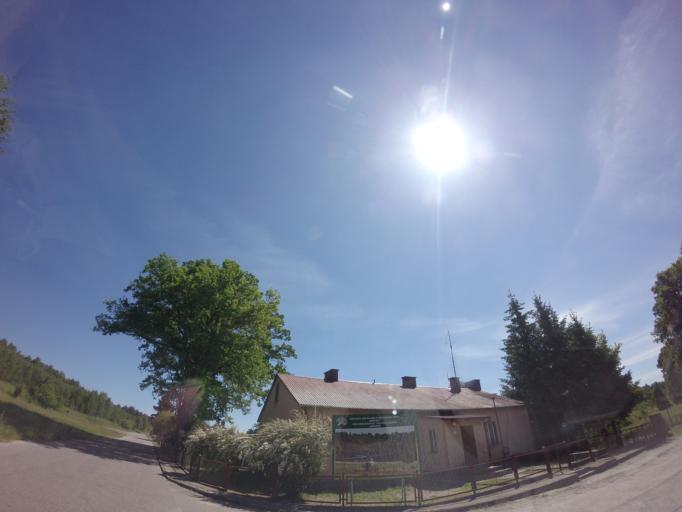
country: PL
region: West Pomeranian Voivodeship
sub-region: Powiat choszczenski
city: Drawno
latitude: 53.3163
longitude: 15.6919
